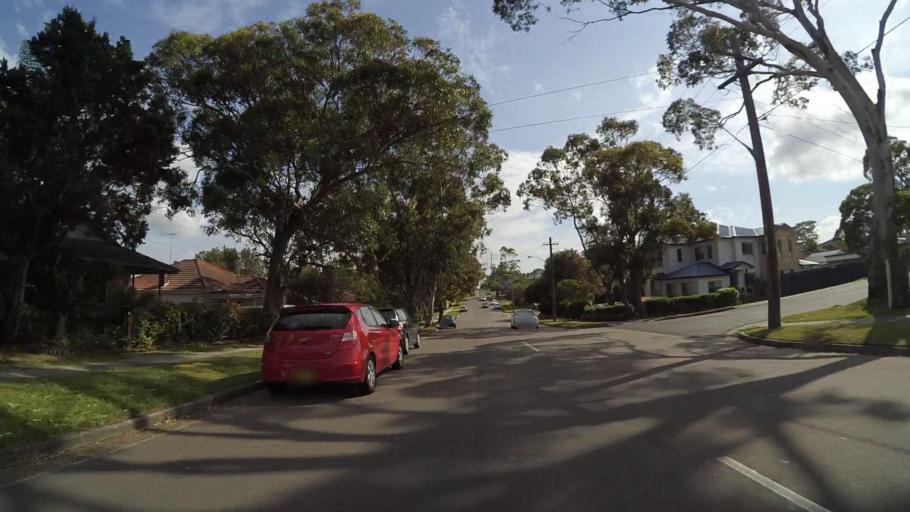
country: AU
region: New South Wales
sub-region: Sutherland Shire
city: Caringbah
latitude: -34.0477
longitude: 151.1173
